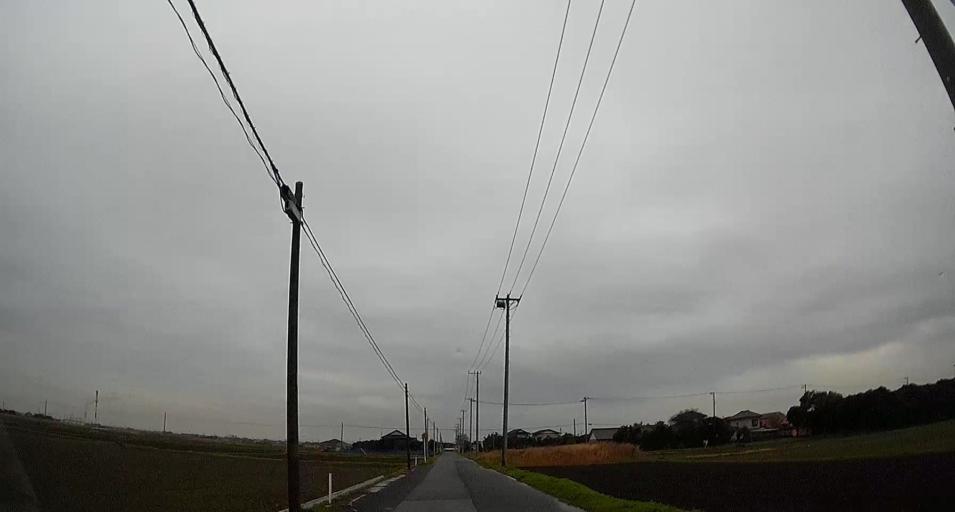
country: JP
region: Chiba
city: Kisarazu
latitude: 35.4225
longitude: 139.9057
